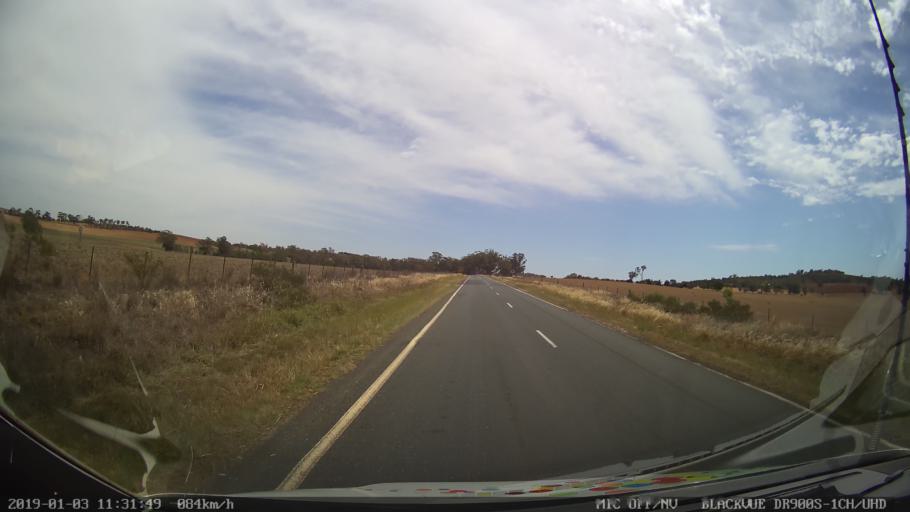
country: AU
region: New South Wales
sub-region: Weddin
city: Grenfell
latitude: -33.9660
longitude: 148.1815
